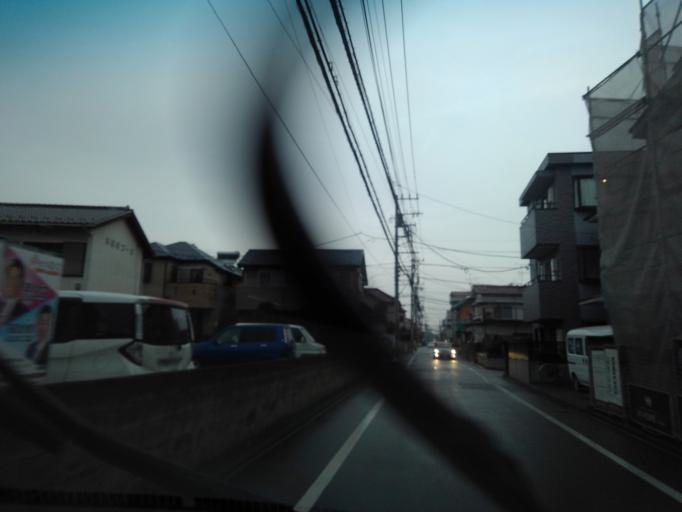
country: JP
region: Tokyo
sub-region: Machida-shi
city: Machida
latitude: 35.5130
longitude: 139.4421
